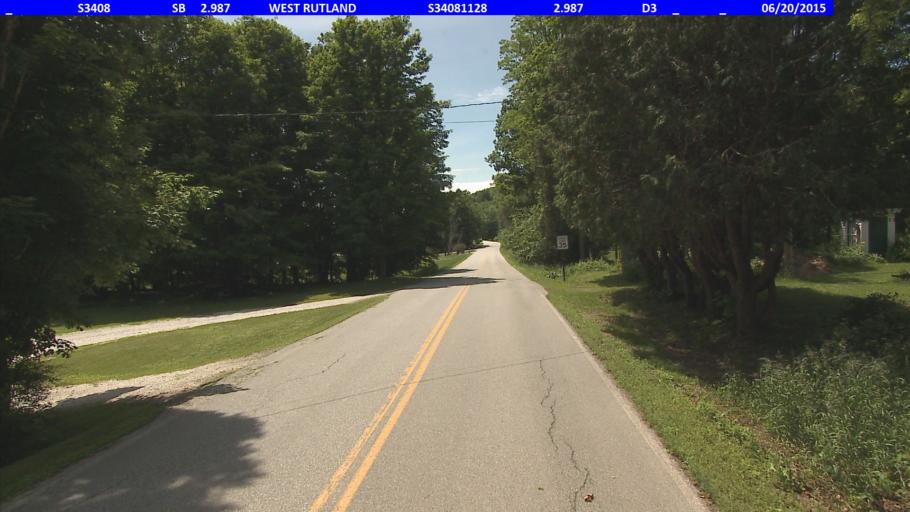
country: US
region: Vermont
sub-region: Rutland County
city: West Rutland
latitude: 43.6518
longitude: -73.0734
